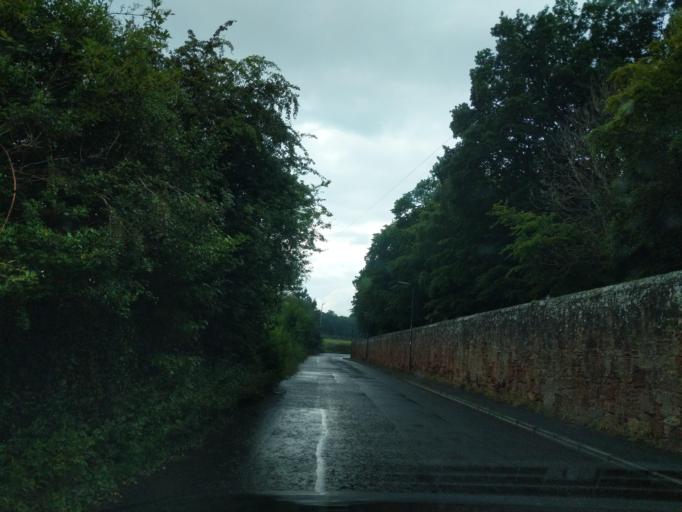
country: GB
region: Scotland
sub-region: Midlothian
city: Dalkeith
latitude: 55.8975
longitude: -3.0793
